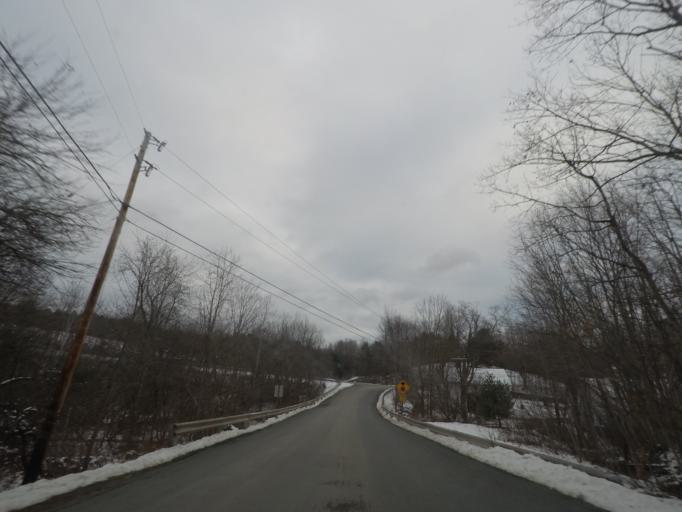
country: US
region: New York
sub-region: Rensselaer County
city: Averill Park
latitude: 42.6394
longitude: -73.5374
